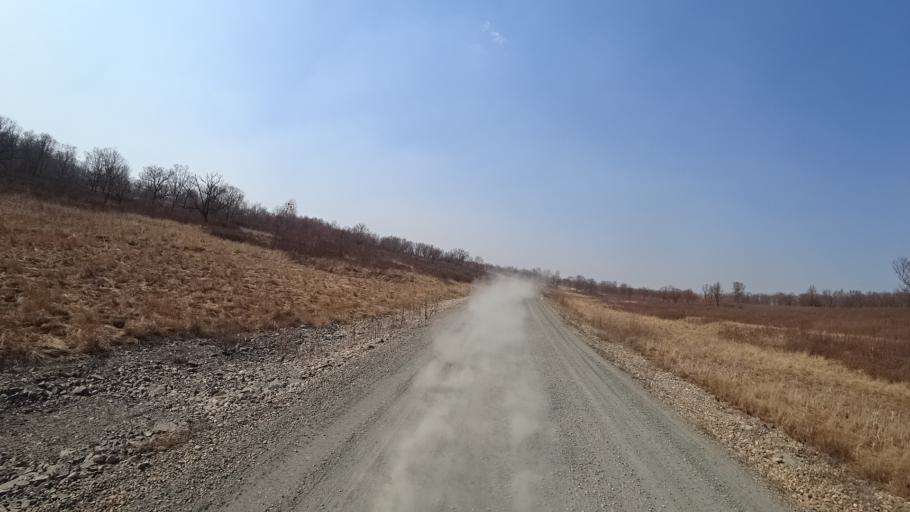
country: RU
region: Amur
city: Novobureyskiy
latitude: 49.8234
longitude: 129.9969
